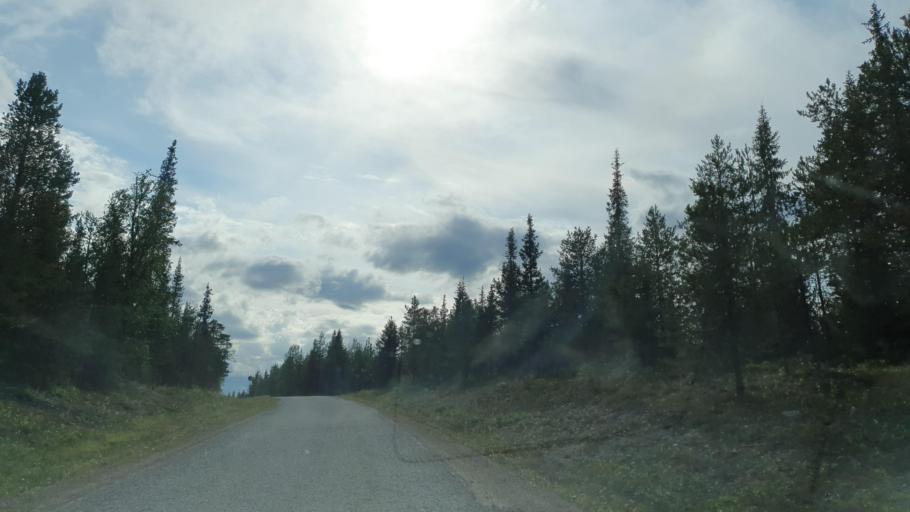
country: FI
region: Lapland
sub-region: Tunturi-Lappi
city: Muonio
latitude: 67.7034
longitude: 24.1206
